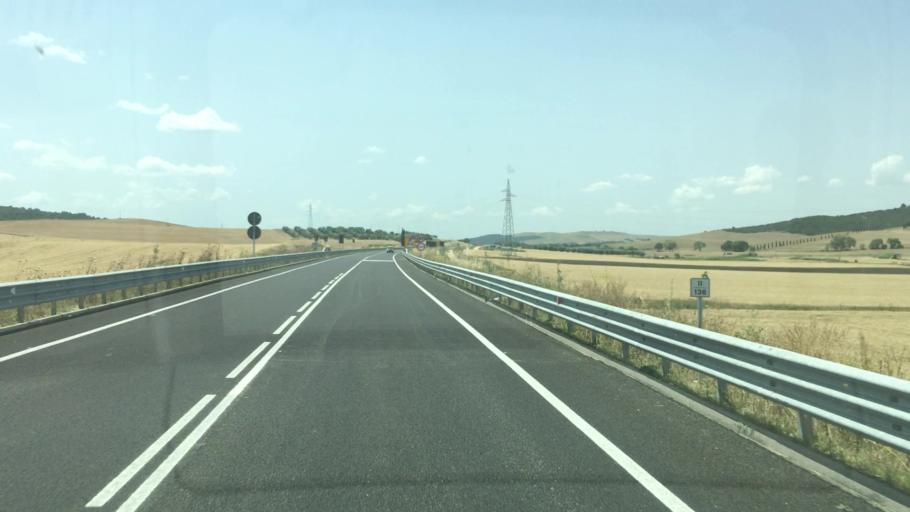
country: IT
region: Basilicate
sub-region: Provincia di Matera
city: La Martella
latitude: 40.6718
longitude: 16.5048
